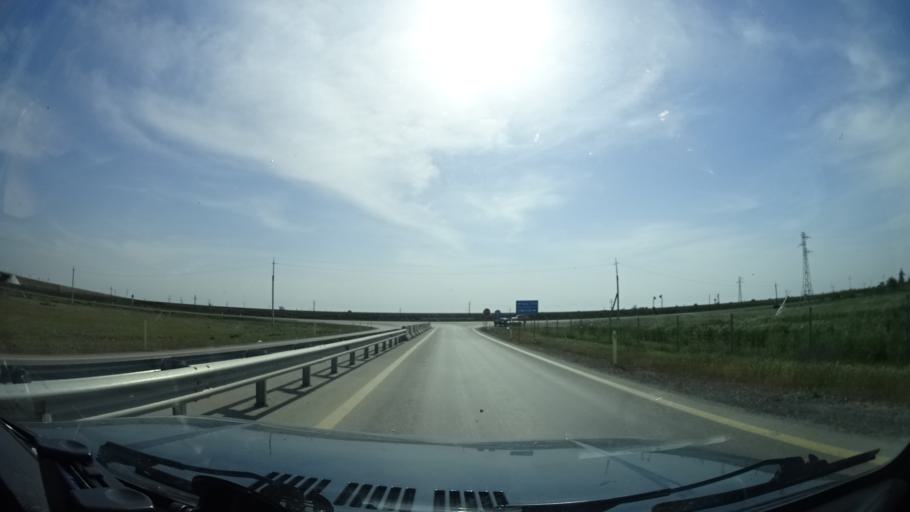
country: AZ
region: Salyan
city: Salyan
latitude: 39.6219
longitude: 48.9471
